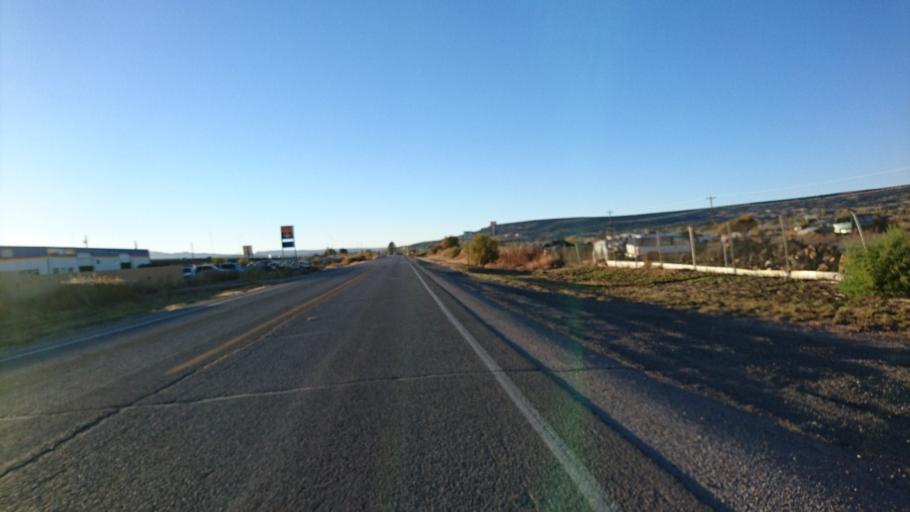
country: US
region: New Mexico
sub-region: Cibola County
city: Grants
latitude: 35.1376
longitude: -107.8243
